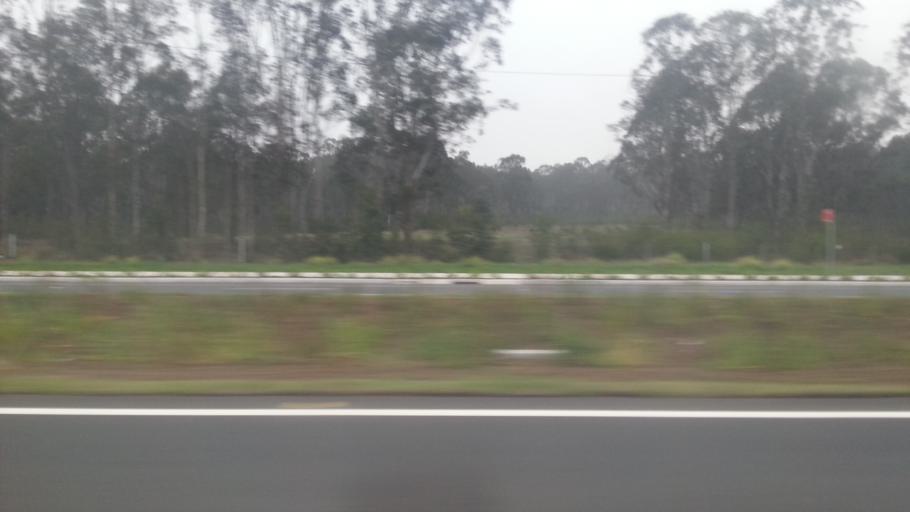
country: AU
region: New South Wales
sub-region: Camden
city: Narellan
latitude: -34.0182
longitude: 150.7244
